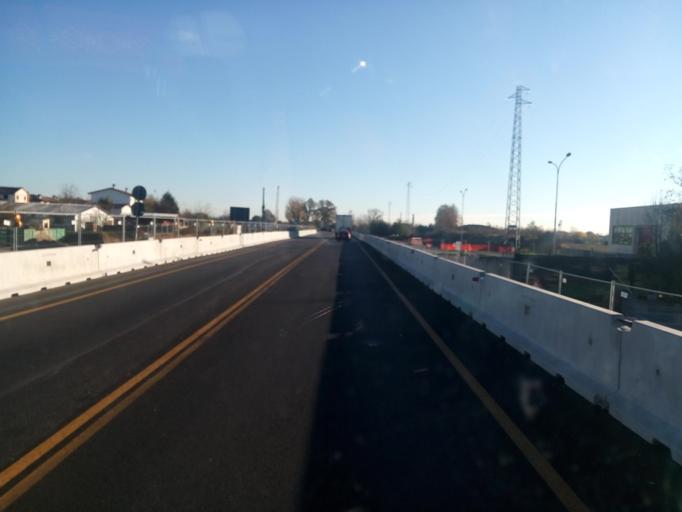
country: IT
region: Veneto
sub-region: Provincia di Vicenza
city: Marostica
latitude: 45.7276
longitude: 11.6545
